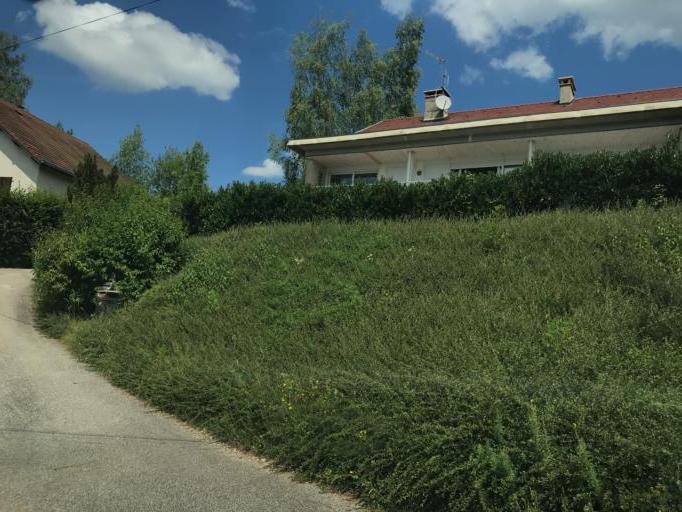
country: FR
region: Franche-Comte
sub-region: Departement du Jura
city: Clairvaux-les-Lacs
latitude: 46.5694
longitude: 5.7600
